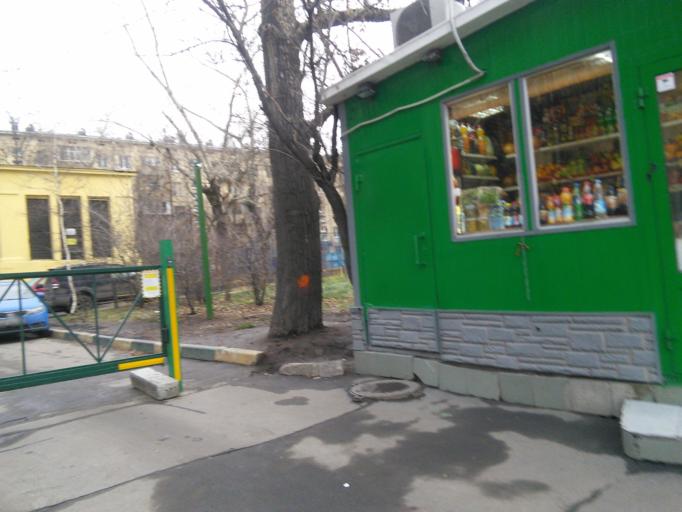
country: RU
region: Moscow
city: Sokol
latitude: 55.7985
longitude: 37.5379
